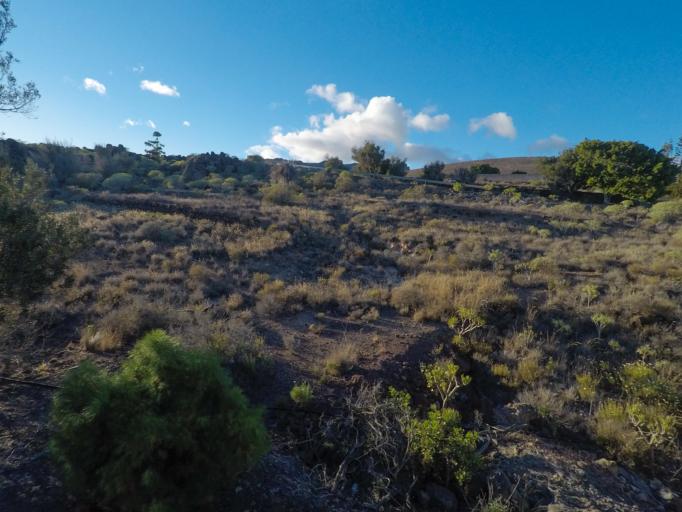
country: ES
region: Canary Islands
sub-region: Provincia de Santa Cruz de Tenerife
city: Alajero
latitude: 28.0485
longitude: -17.1973
